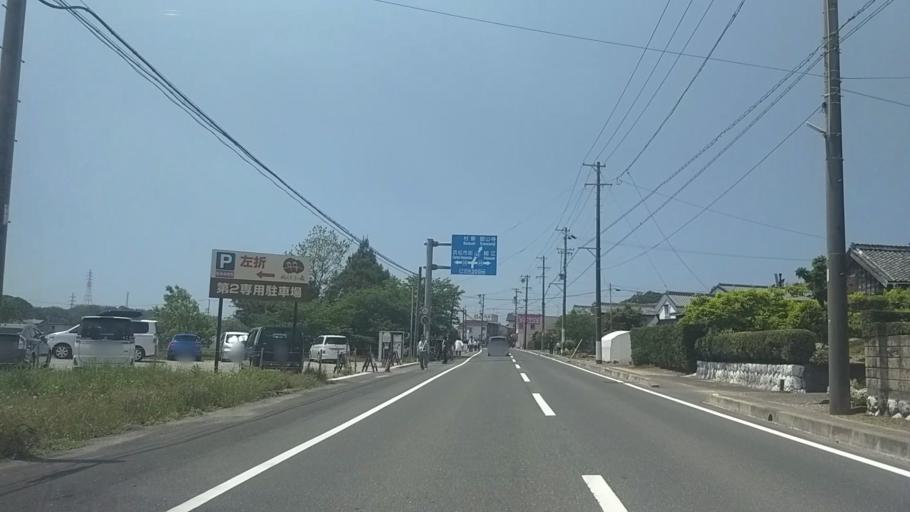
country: JP
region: Shizuoka
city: Hamamatsu
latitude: 34.7647
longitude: 137.6594
